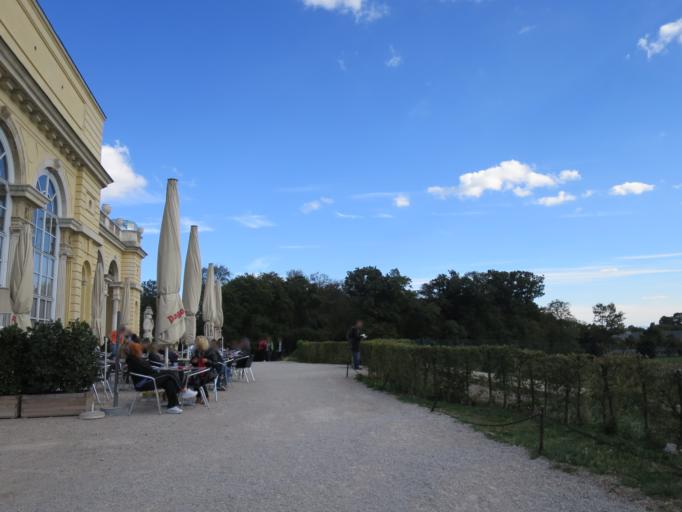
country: AT
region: Lower Austria
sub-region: Politischer Bezirk Modling
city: Vosendorf
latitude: 48.1782
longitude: 16.3084
